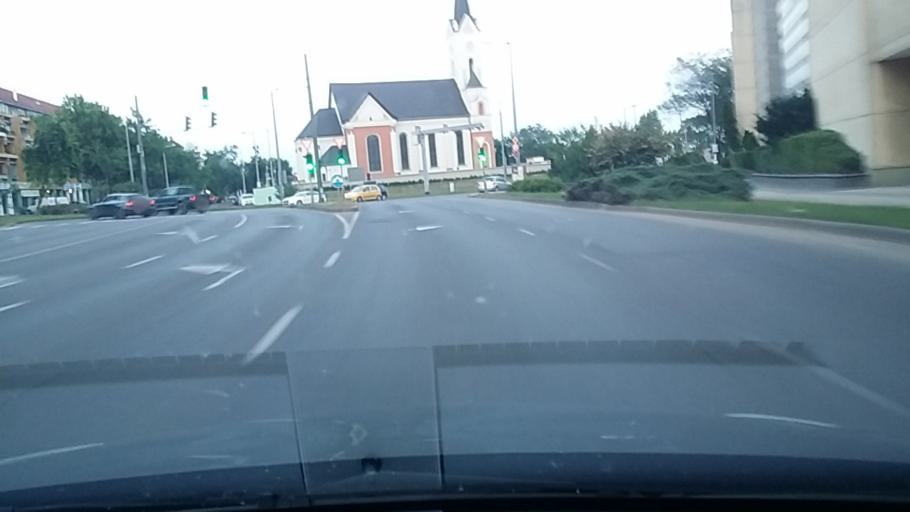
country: HU
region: Borsod-Abauj-Zemplen
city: Miskolc
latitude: 48.1069
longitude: 20.7885
